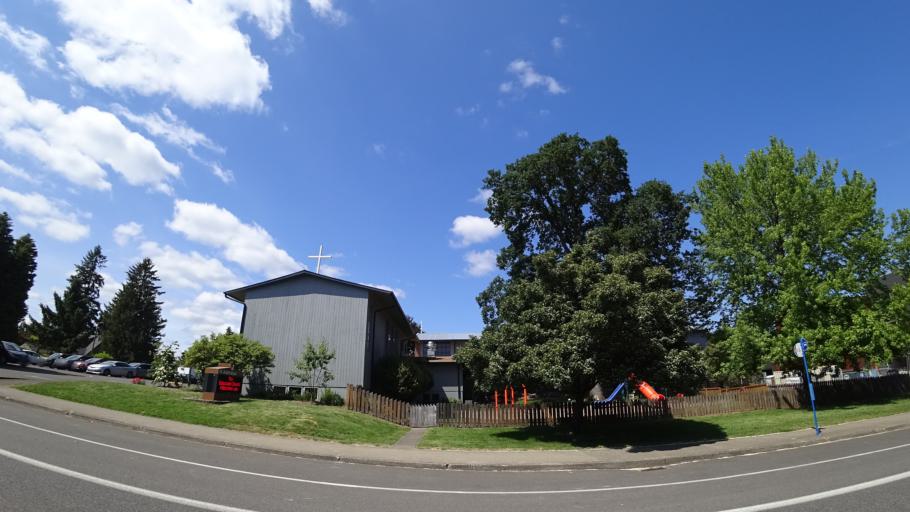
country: US
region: Oregon
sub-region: Multnomah County
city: Portland
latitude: 45.4760
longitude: -122.7000
